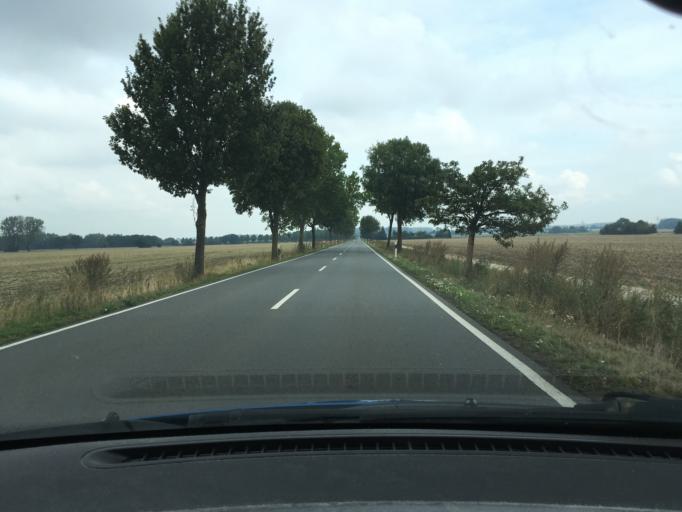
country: DE
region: Lower Saxony
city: Barsinghausen
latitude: 52.3223
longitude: 9.4671
